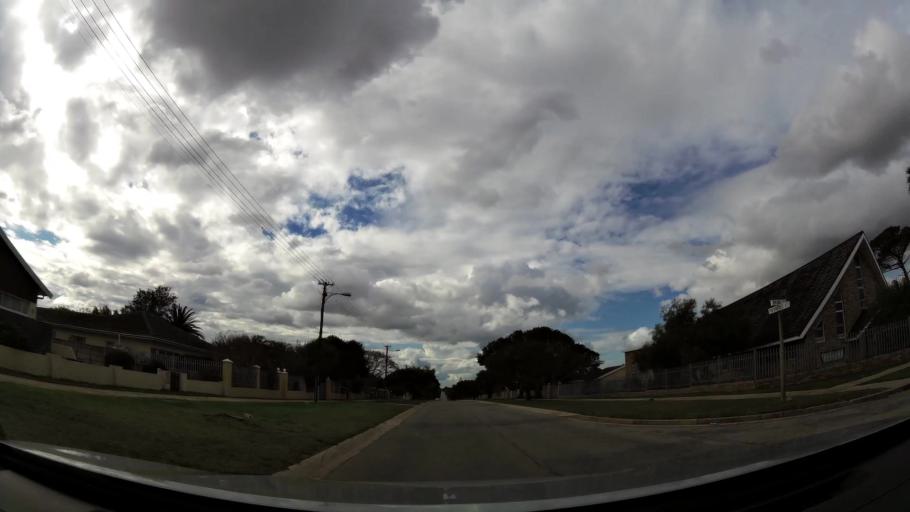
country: ZA
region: Eastern Cape
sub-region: Nelson Mandela Bay Metropolitan Municipality
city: Port Elizabeth
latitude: -33.9431
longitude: 25.5183
